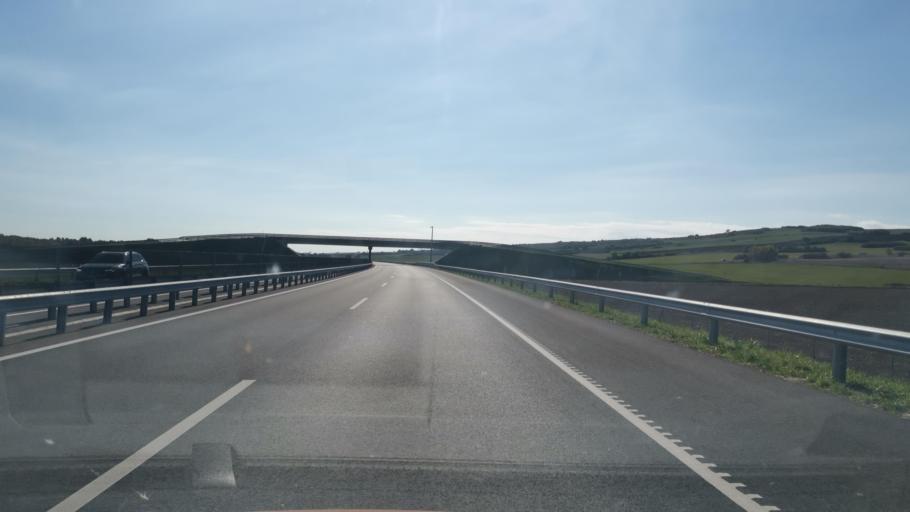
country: HU
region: Borsod-Abauj-Zemplen
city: Szikszo
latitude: 48.1969
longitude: 20.9068
